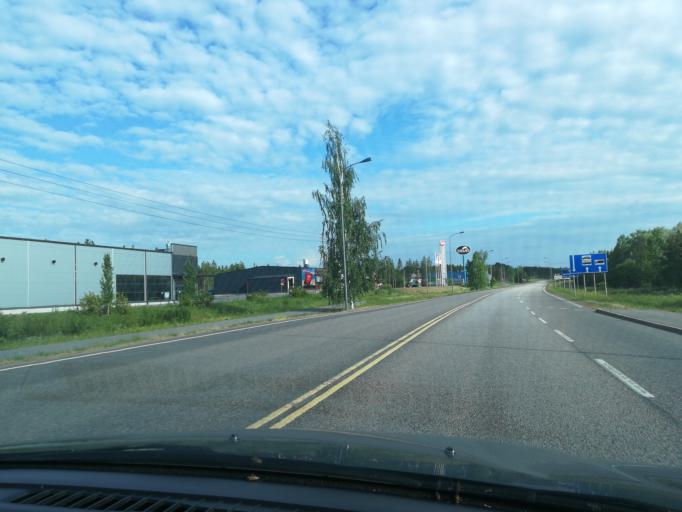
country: FI
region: South Karelia
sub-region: Imatra
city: Imatra
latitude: 61.1511
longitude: 28.8082
